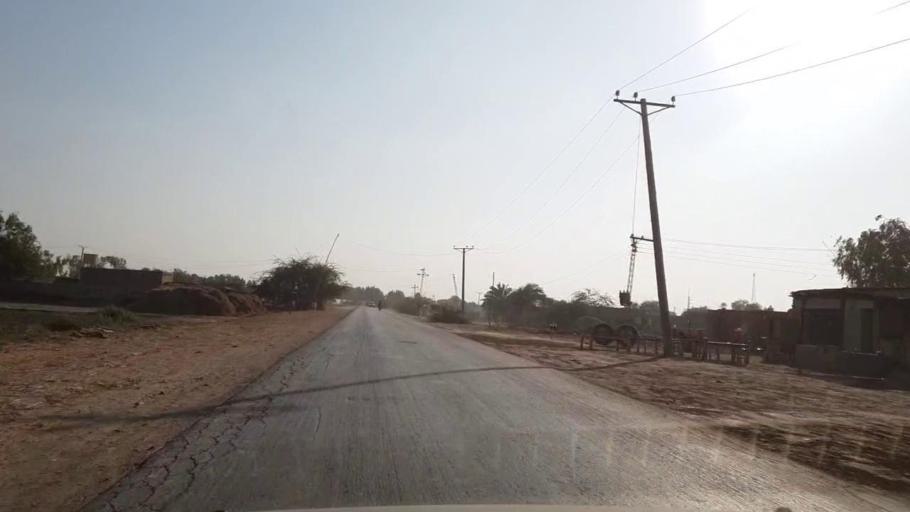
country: PK
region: Sindh
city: Bulri
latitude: 24.8673
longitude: 68.3380
